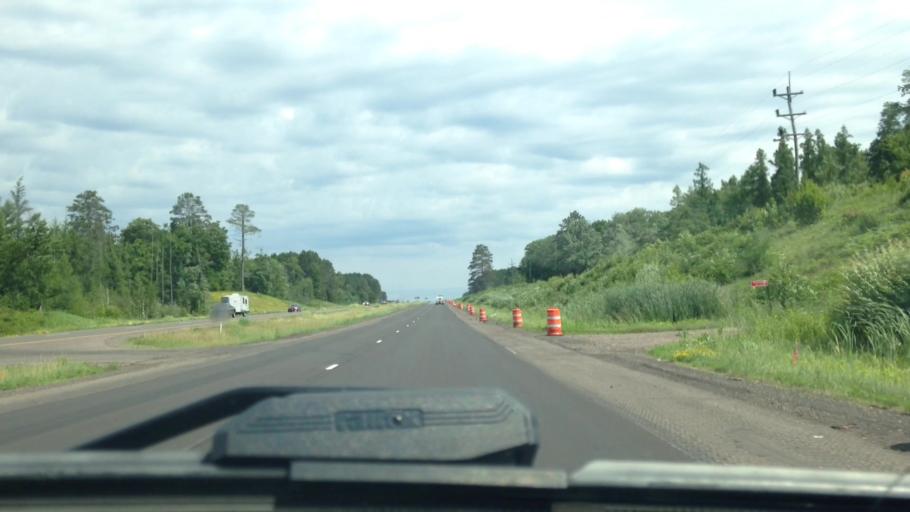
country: US
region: Wisconsin
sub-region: Washburn County
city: Spooner
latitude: 46.1444
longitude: -91.8140
